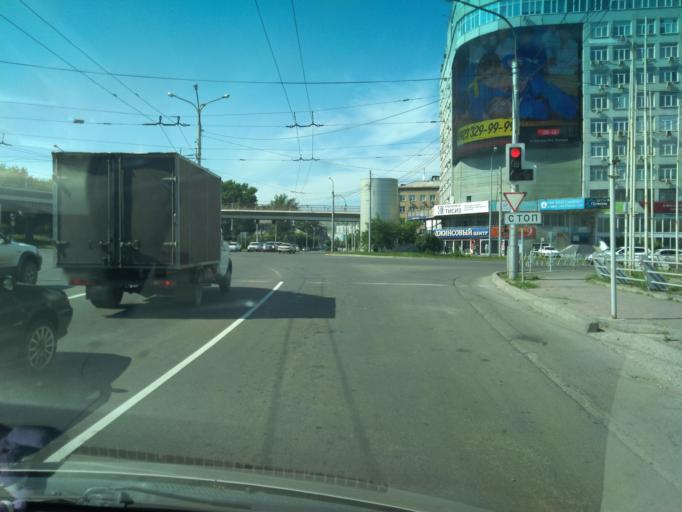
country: RU
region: Krasnoyarskiy
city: Krasnoyarsk
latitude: 56.0244
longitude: 92.8338
